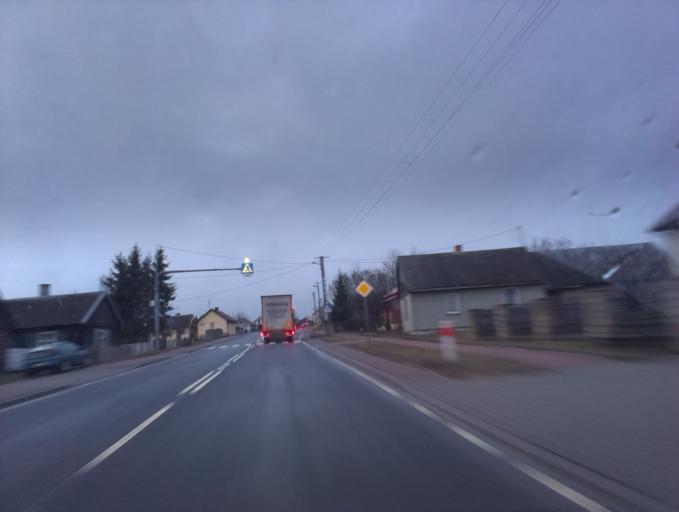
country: PL
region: Lodz Voivodeship
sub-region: Powiat opoczynski
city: Zarnow
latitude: 51.2098
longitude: 20.1971
